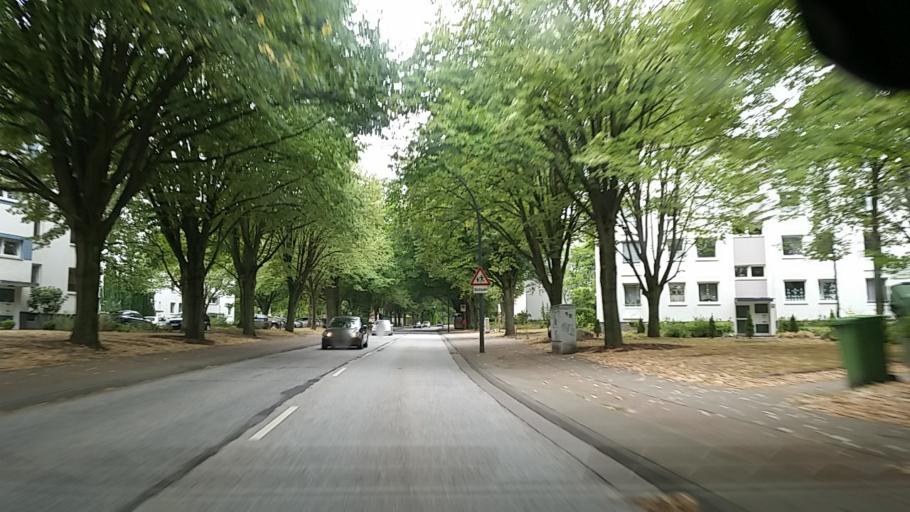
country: DE
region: Hamburg
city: Bergedorf
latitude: 53.5048
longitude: 10.2196
